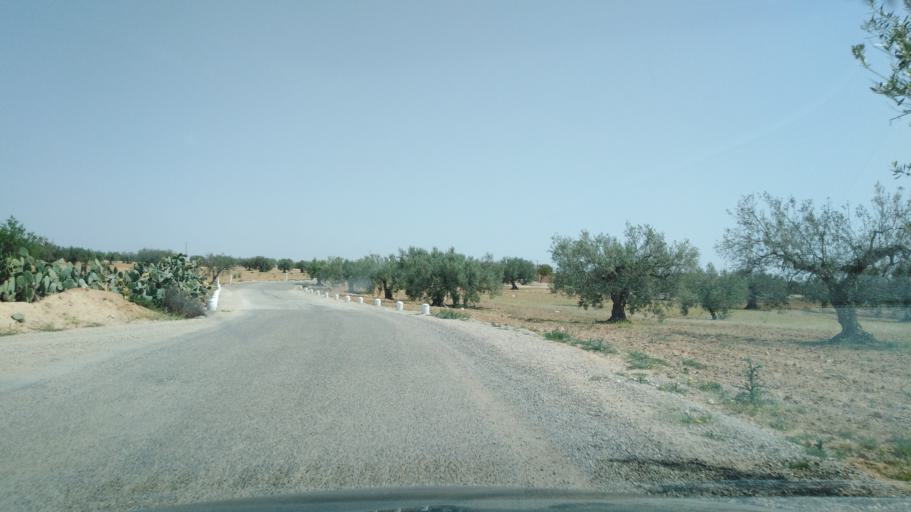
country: TN
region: Safaqis
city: Sfax
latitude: 34.6853
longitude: 10.4411
